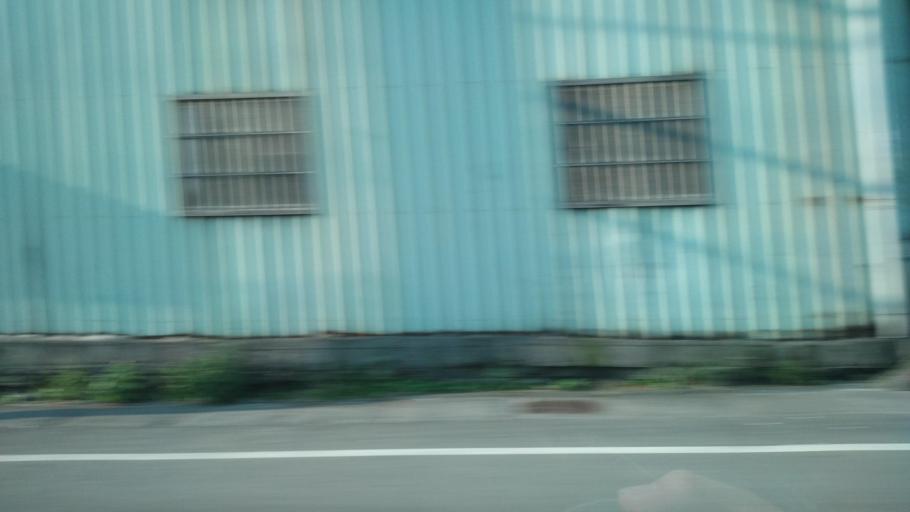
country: TW
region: Taipei
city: Taipei
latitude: 25.2595
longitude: 121.4998
